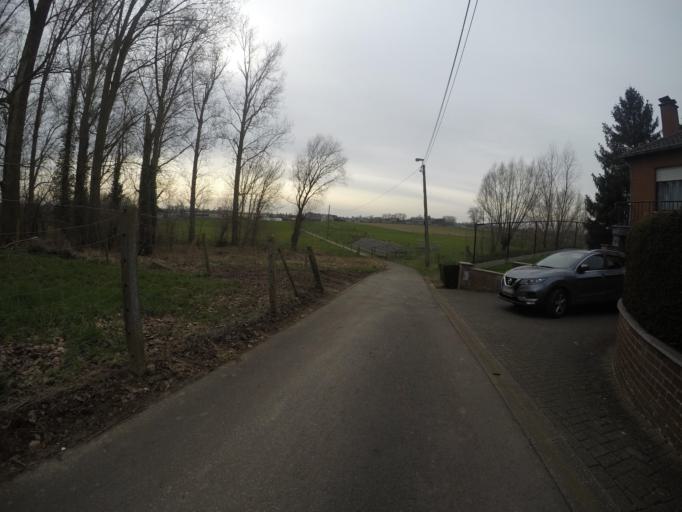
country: BE
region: Flanders
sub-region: Provincie Oost-Vlaanderen
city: Sint-Maria-Lierde
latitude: 50.8211
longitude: 3.8449
